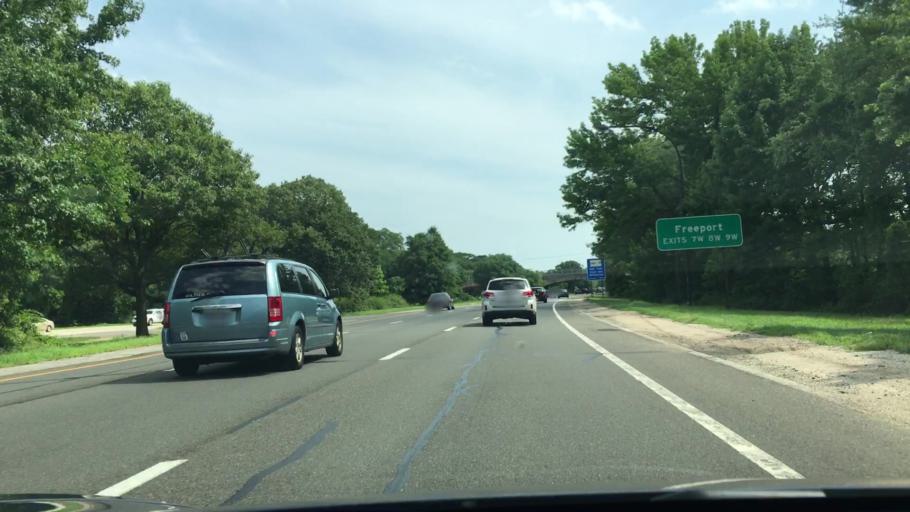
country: US
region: New York
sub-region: Nassau County
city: North Merrick
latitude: 40.6825
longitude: -73.5726
